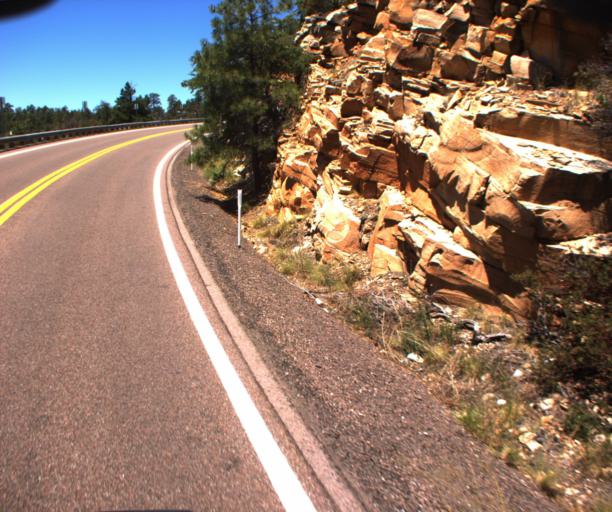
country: US
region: Arizona
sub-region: Gila County
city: Pine
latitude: 34.4197
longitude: -111.5060
